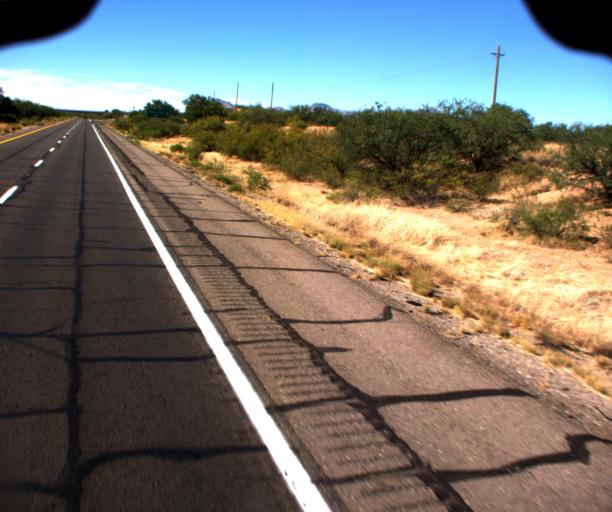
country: US
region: Arizona
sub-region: Pima County
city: Arivaca Junction
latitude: 31.6834
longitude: -111.0647
